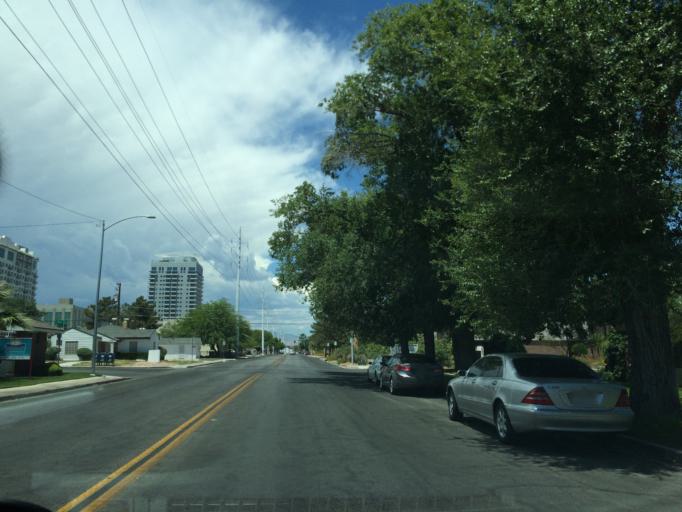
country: US
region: Nevada
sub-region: Clark County
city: Las Vegas
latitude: 36.1599
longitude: -115.1432
